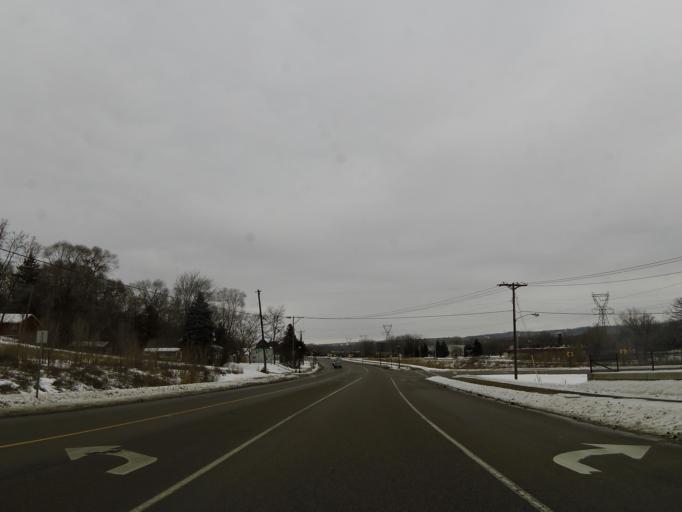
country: US
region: Minnesota
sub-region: Dakota County
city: Inver Grove Heights
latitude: 44.8508
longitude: -93.0200
